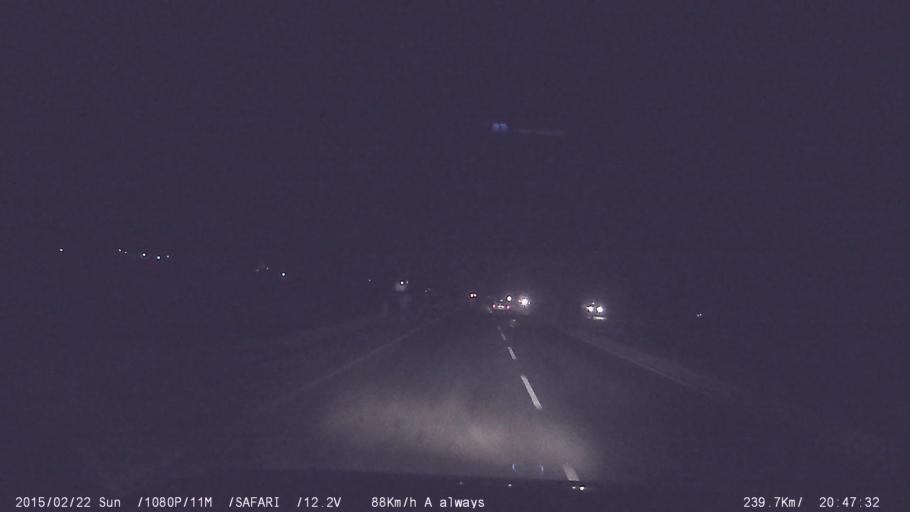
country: IN
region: Tamil Nadu
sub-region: Dindigul
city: Vedasandur
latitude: 10.4961
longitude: 77.9449
